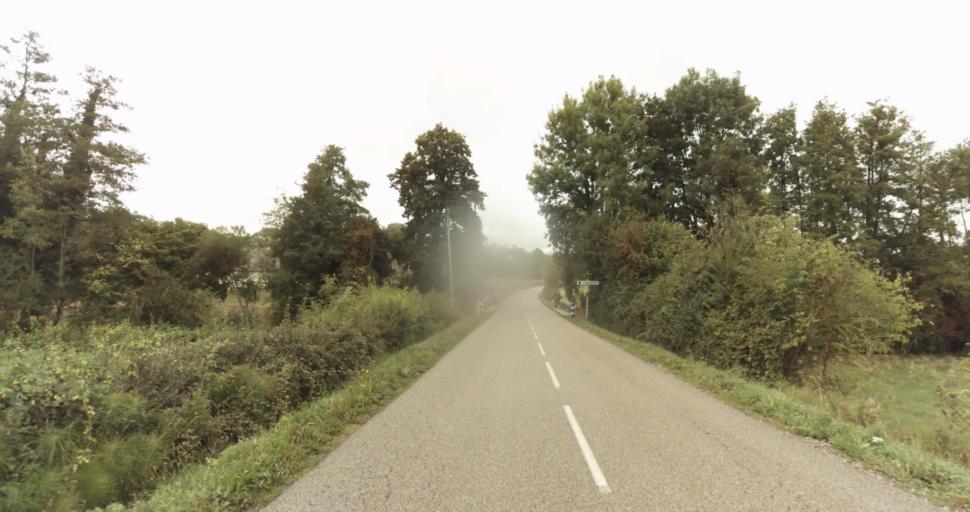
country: FR
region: Lower Normandy
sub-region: Departement de l'Orne
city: Vimoutiers
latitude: 48.9124
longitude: 0.2024
